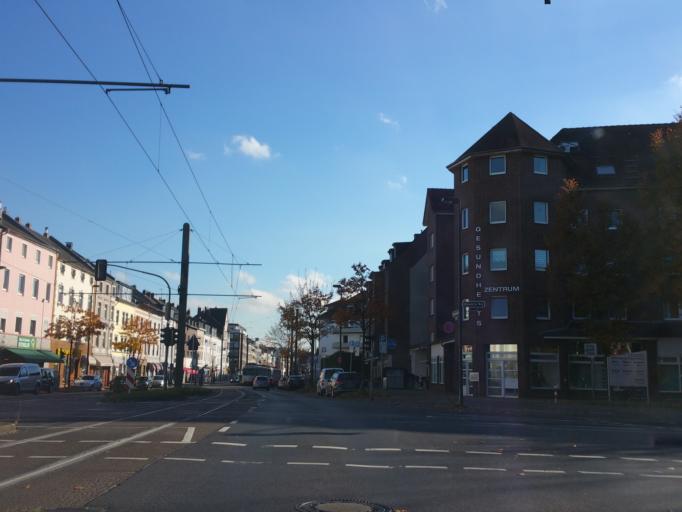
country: DE
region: North Rhine-Westphalia
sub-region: Regierungsbezirk Dusseldorf
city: Dusseldorf
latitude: 51.1909
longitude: 6.8158
